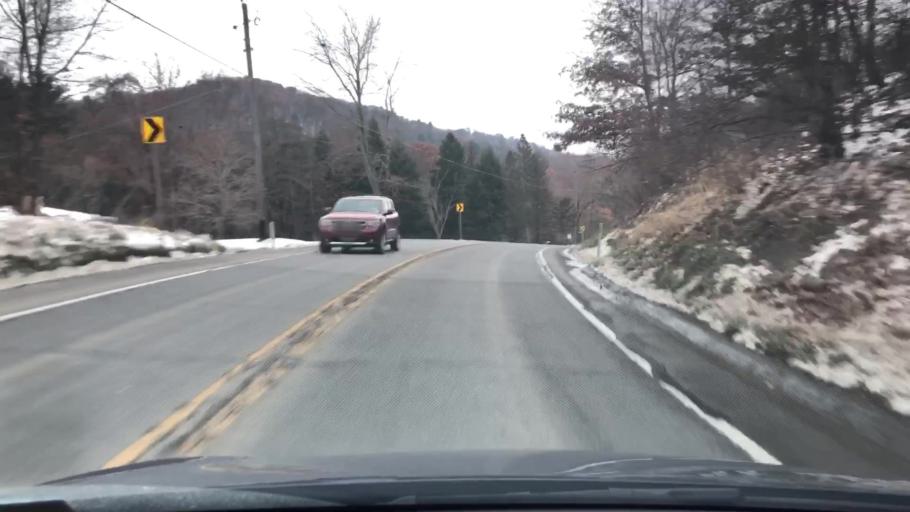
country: US
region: Pennsylvania
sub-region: Jefferson County
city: Brookville
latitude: 41.1274
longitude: -79.1635
